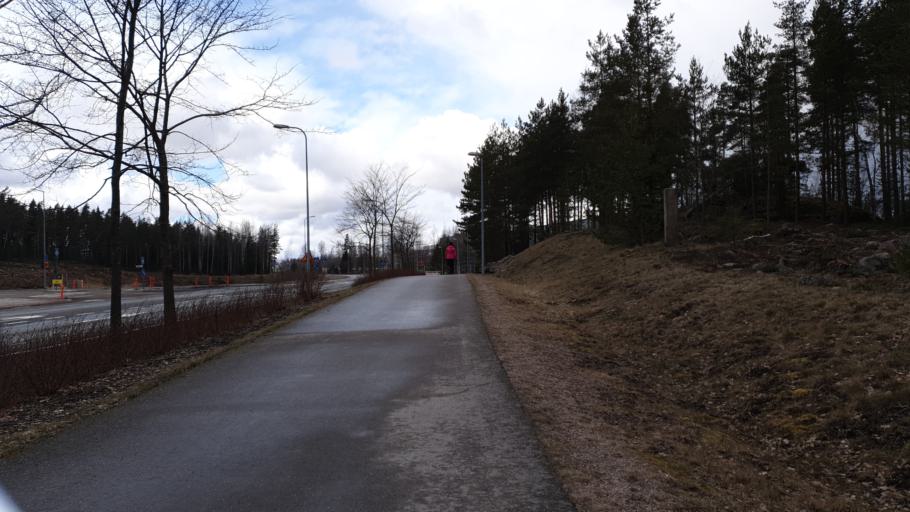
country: FI
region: Uusimaa
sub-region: Helsinki
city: Vantaa
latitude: 60.2920
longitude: 24.9319
